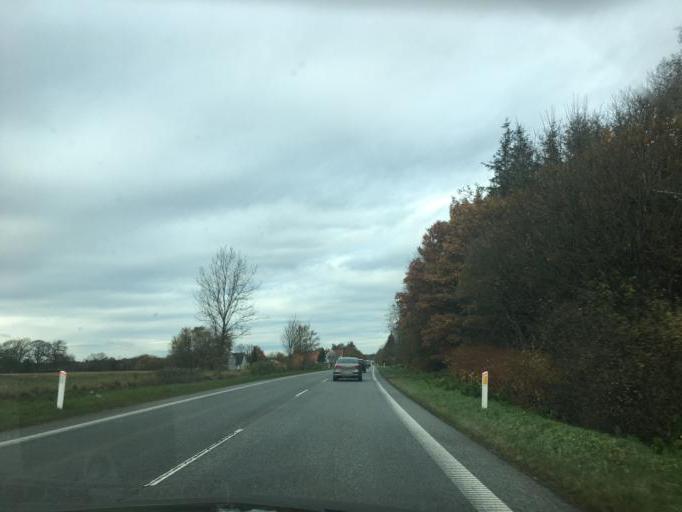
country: DK
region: South Denmark
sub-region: Vejle Kommune
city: Vejle
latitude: 55.6243
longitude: 9.4938
